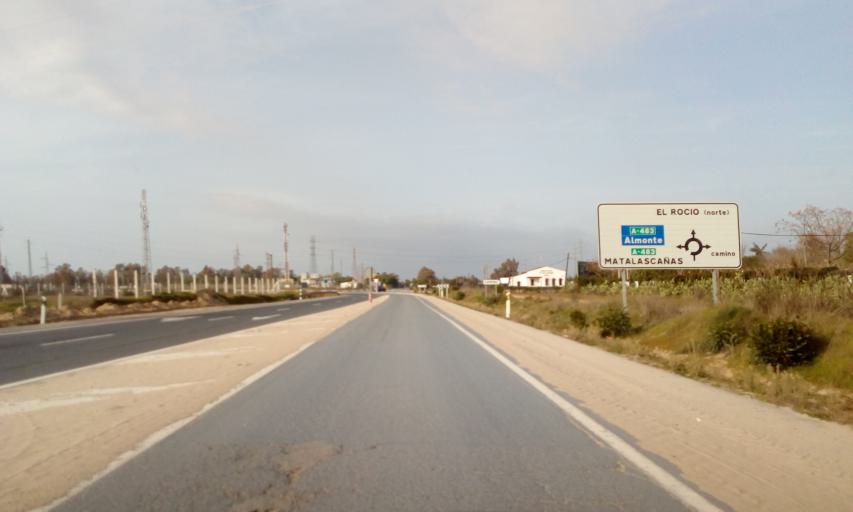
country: ES
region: Andalusia
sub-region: Provincia de Huelva
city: Almonte
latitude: 37.1403
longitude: -6.4909
